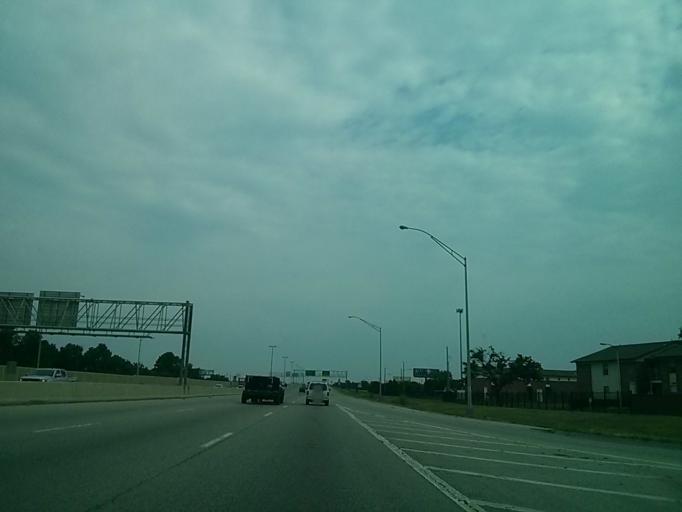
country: US
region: Oklahoma
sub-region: Tulsa County
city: Broken Arrow
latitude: 36.1420
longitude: -95.8600
